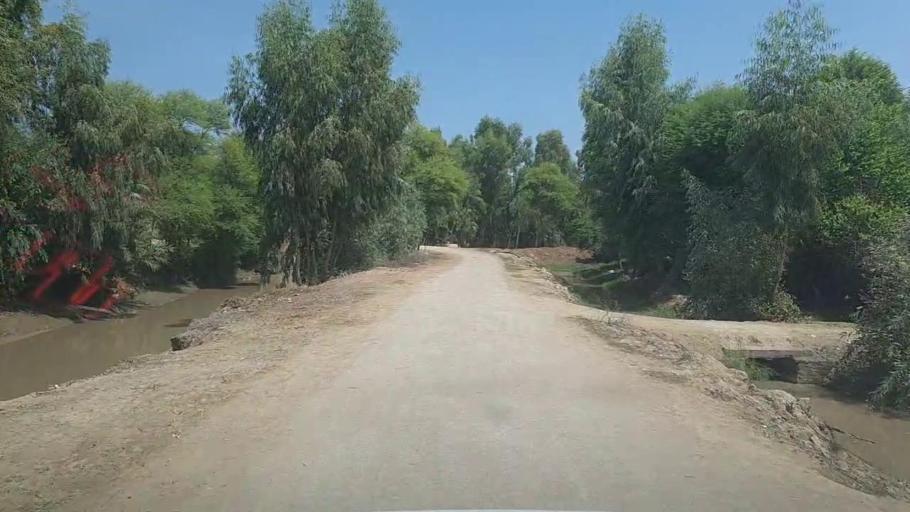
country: PK
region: Sindh
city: Kandhkot
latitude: 28.2682
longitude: 69.2122
